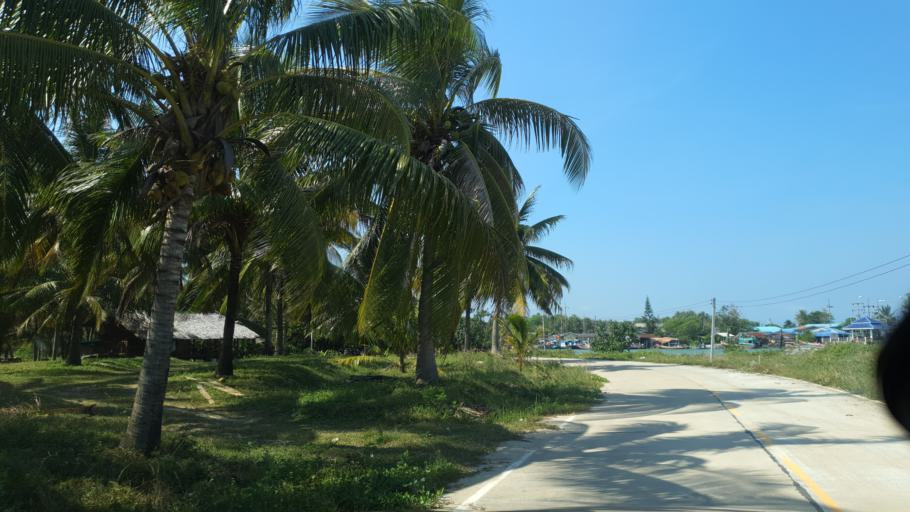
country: TH
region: Surat Thani
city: Tha Chana
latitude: 9.6008
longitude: 99.2084
